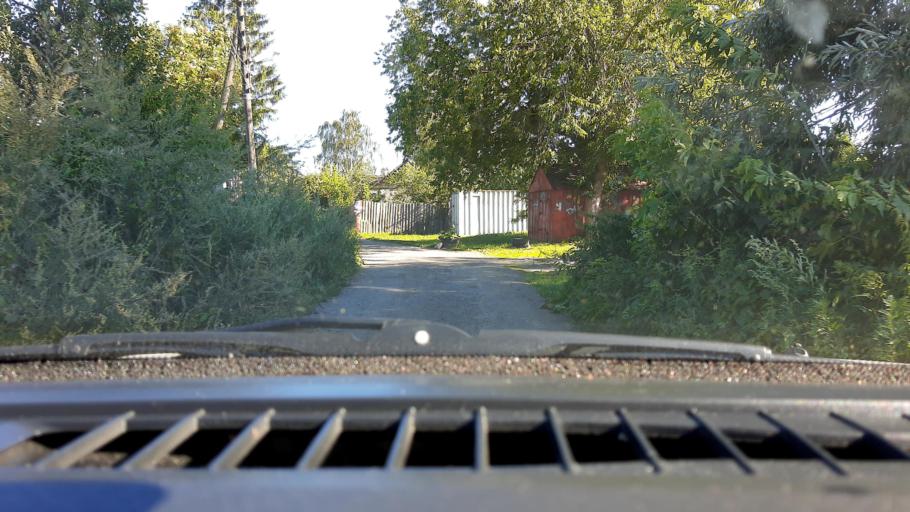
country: RU
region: Nizjnij Novgorod
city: Gorbatovka
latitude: 56.3616
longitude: 43.8373
